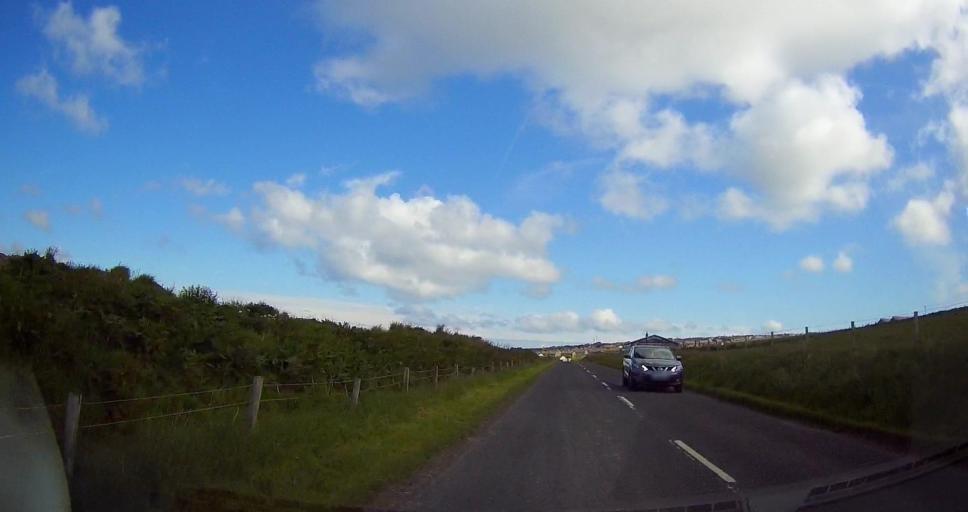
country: GB
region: Scotland
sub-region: Orkney Islands
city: Orkney
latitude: 58.9682
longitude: -2.9637
